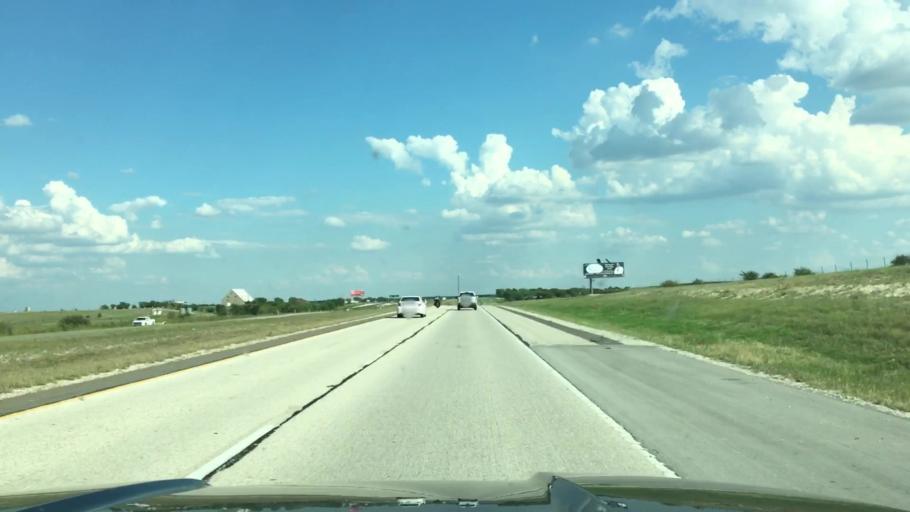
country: US
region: Texas
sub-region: Wise County
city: New Fairview
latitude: 33.1550
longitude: -97.5170
